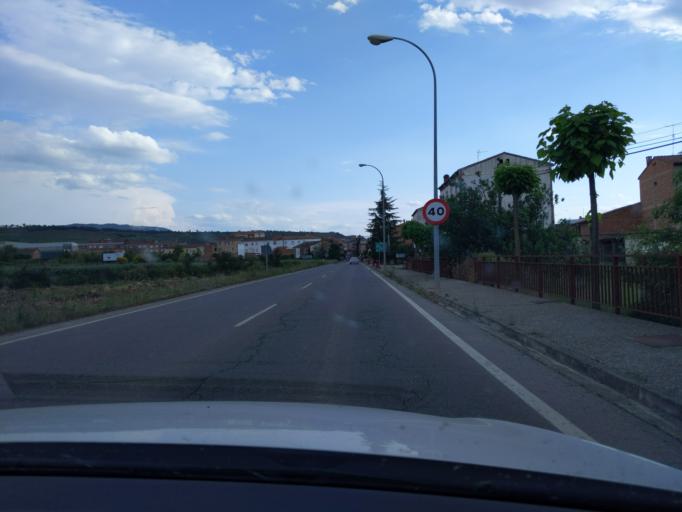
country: ES
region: La Rioja
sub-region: Provincia de La Rioja
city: Alberite
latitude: 42.4099
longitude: -2.4374
